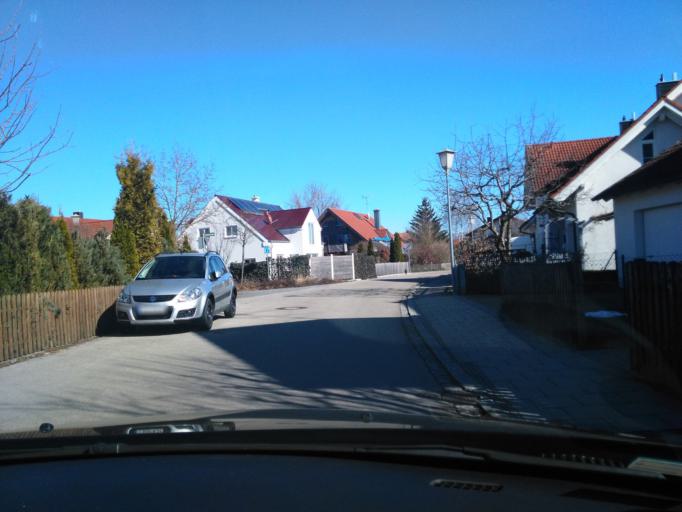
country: DE
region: Bavaria
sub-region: Upper Bavaria
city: Mammendorf
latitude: 48.2134
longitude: 11.1724
